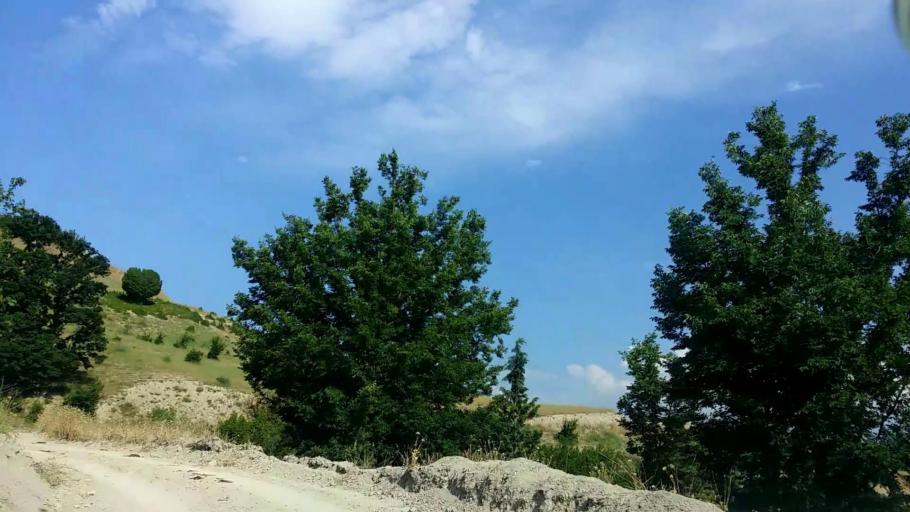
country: IR
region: Mazandaran
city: Chalus
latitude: 36.5475
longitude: 51.2947
